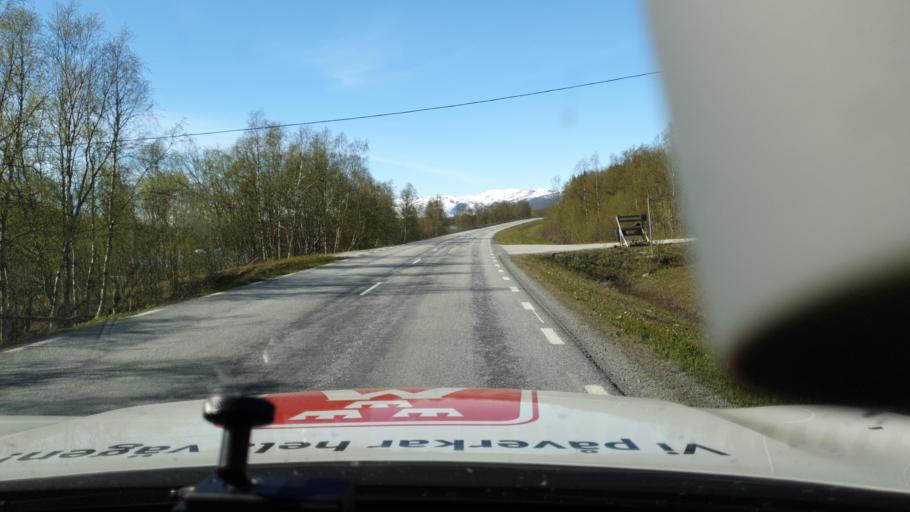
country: NO
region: Nordland
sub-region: Rana
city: Mo i Rana
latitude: 65.7843
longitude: 15.1082
